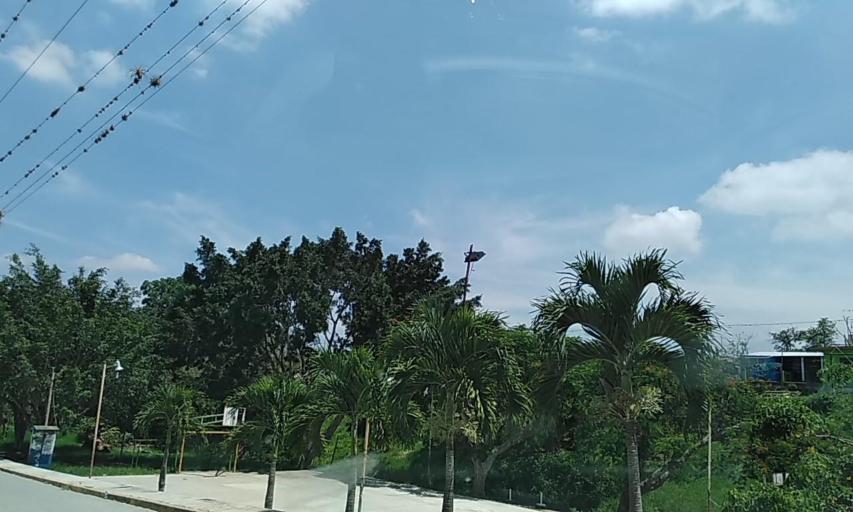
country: MX
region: Veracruz
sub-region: Emiliano Zapata
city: Dos Rios
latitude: 19.4410
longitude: -96.7544
